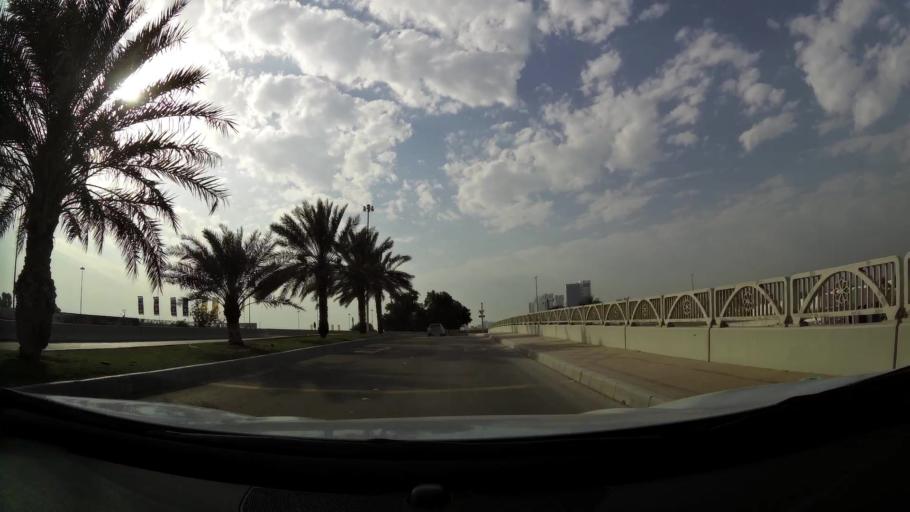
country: AE
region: Abu Dhabi
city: Abu Dhabi
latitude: 24.4080
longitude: 54.4726
